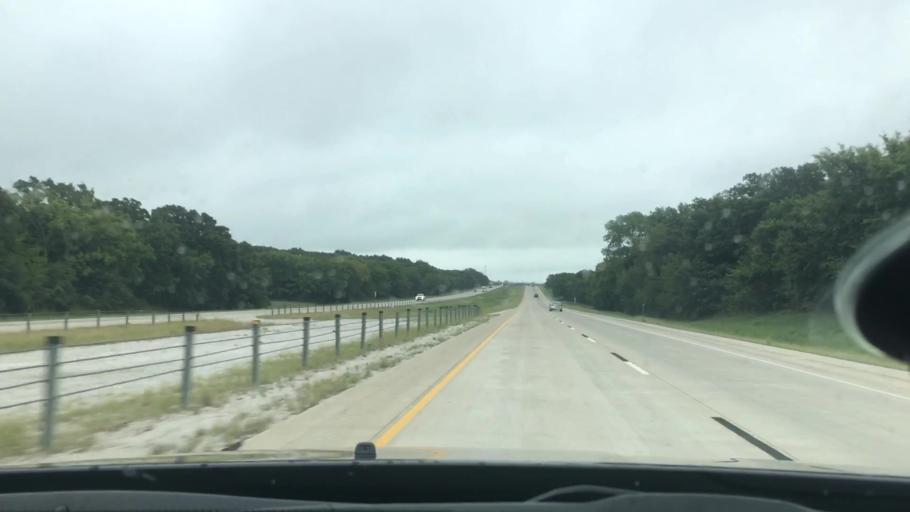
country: US
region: Oklahoma
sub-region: Okmulgee County
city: Wilson
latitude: 35.4275
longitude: -96.0850
